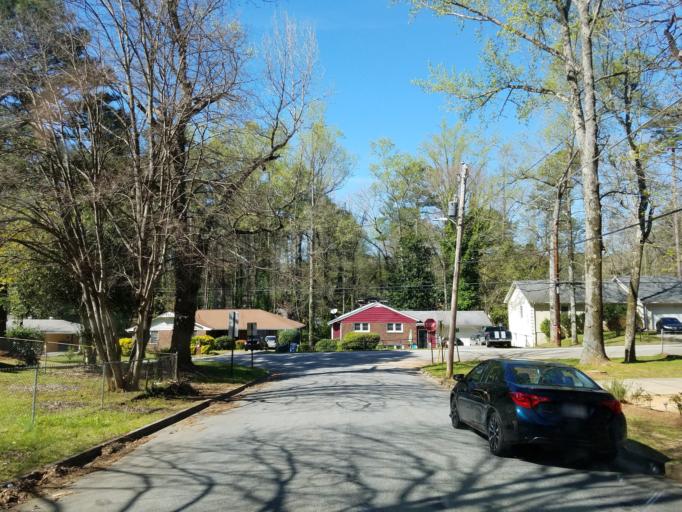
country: US
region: Georgia
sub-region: Fulton County
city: Atlanta
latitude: 33.7633
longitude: -84.4753
